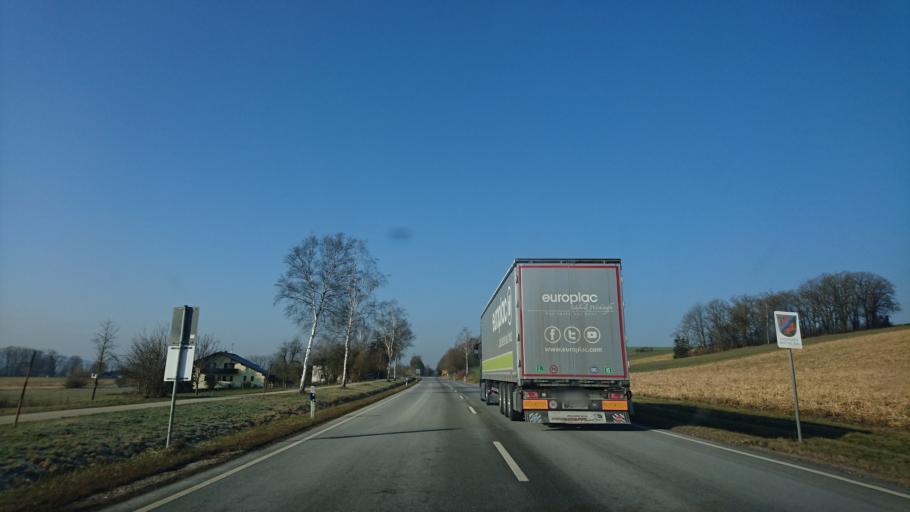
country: DE
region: Bavaria
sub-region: Lower Bavaria
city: Bayerbach
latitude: 48.4212
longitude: 13.1718
